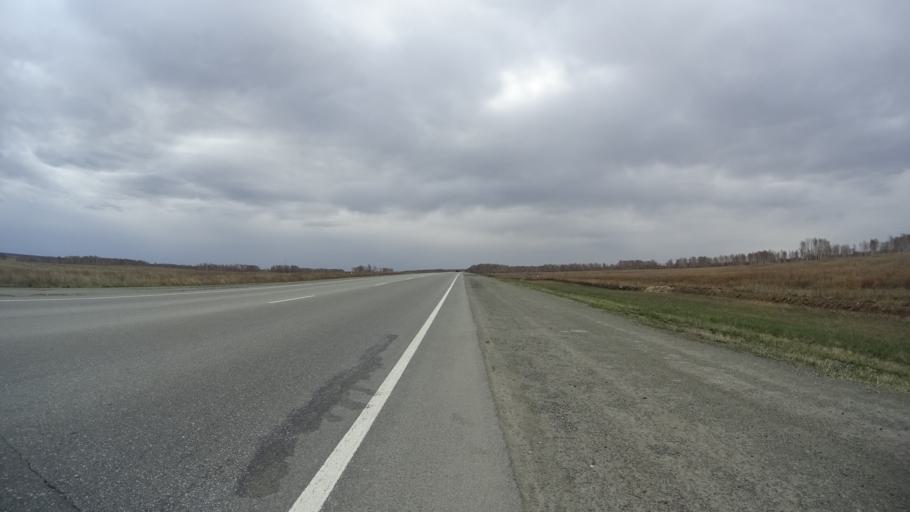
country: RU
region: Chelyabinsk
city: Yemanzhelinsk
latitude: 54.7055
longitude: 61.2562
